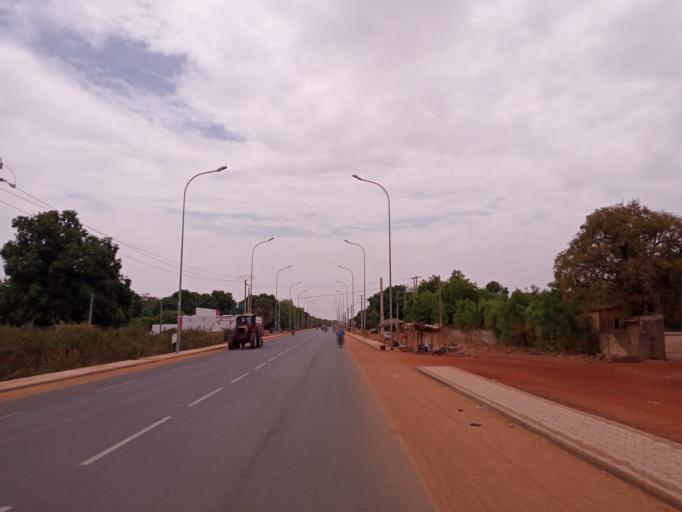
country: ML
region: Koulikoro
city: Koulikoro
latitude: 12.8517
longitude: -7.5706
